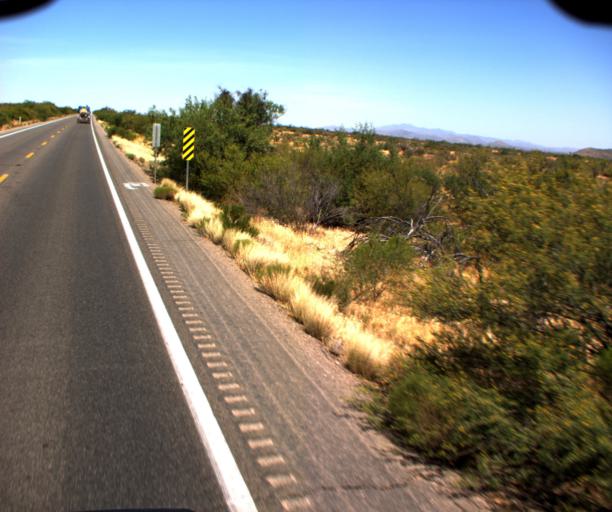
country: US
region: Arizona
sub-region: Gila County
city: Peridot
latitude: 33.3106
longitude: -110.5049
